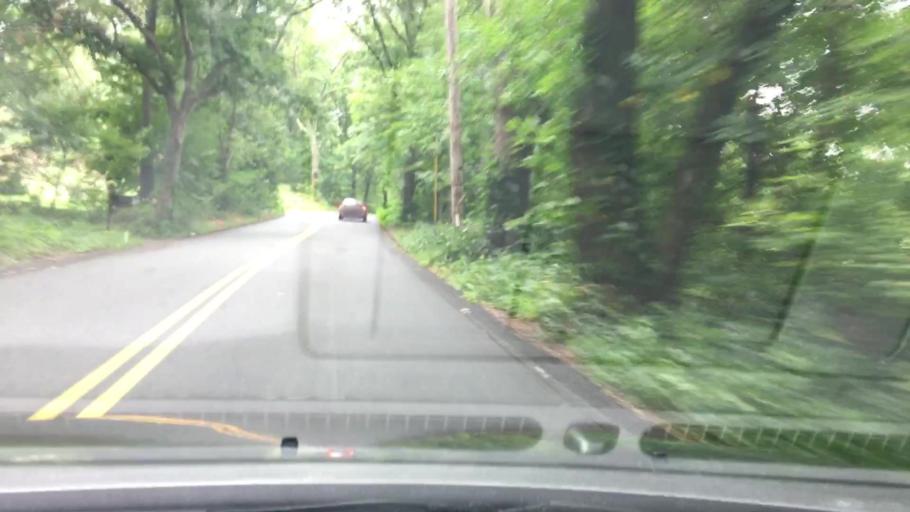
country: US
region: Rhode Island
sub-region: Providence County
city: Cumberland Hill
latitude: 42.0192
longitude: -71.4505
